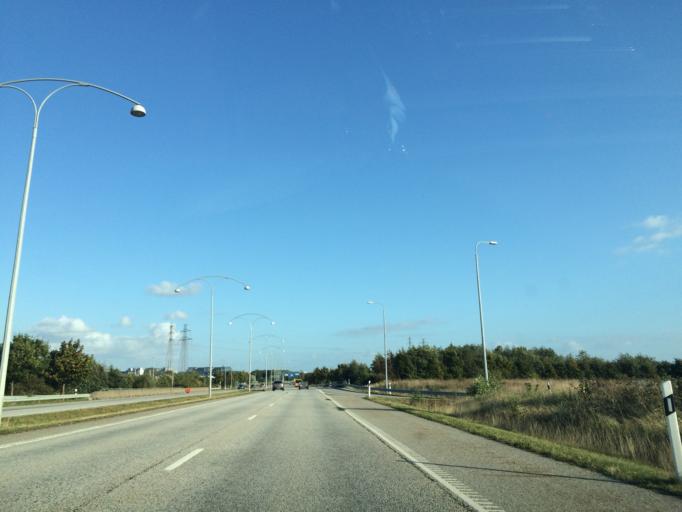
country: SE
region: Skane
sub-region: Lunds Kommun
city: Lund
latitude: 55.7188
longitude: 13.1490
